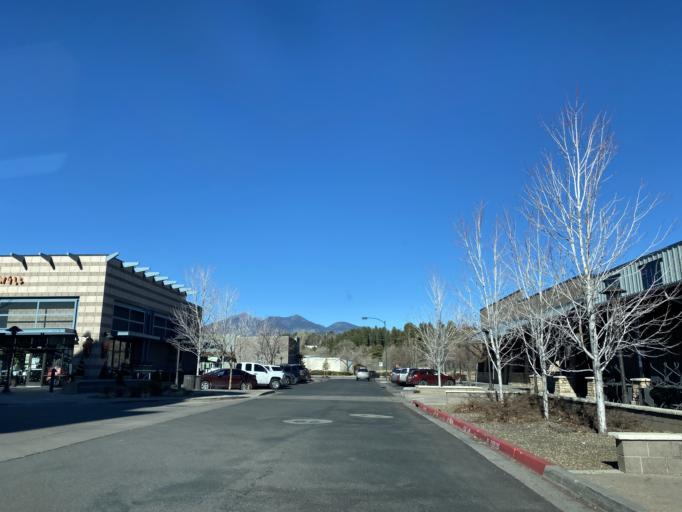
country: US
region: Arizona
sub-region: Coconino County
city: Flagstaff
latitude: 35.1913
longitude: -111.6415
